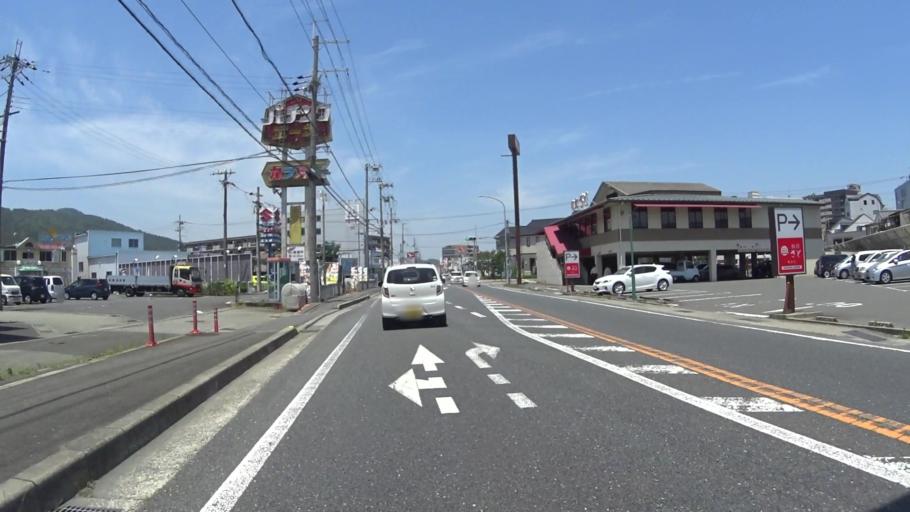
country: JP
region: Kyoto
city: Kameoka
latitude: 35.0298
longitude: 135.5540
